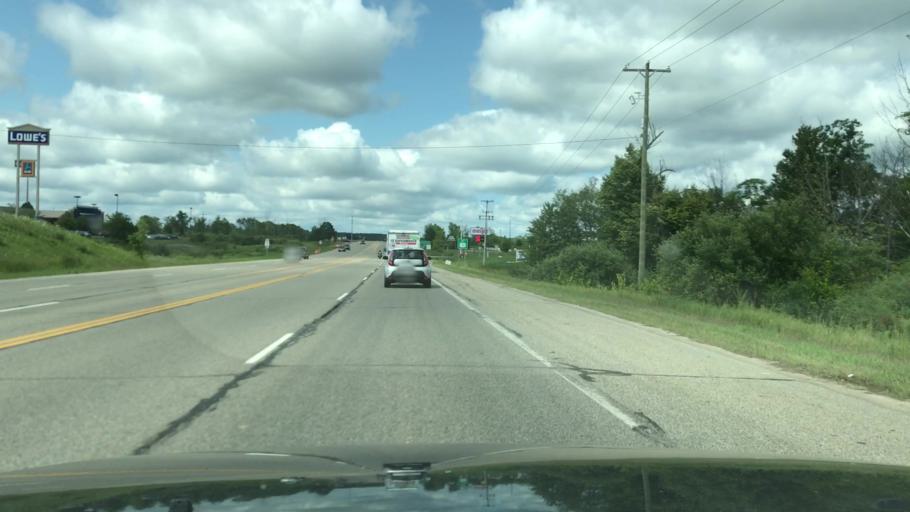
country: US
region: Michigan
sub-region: Mecosta County
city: Big Rapids
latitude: 43.6883
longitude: -85.5124
